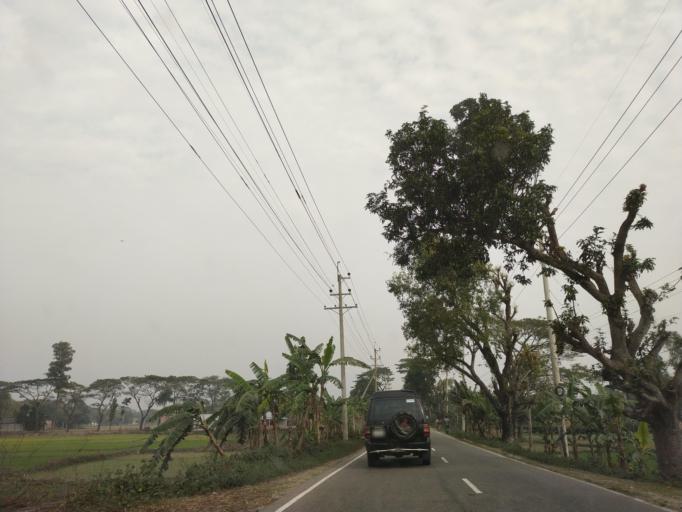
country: BD
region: Dhaka
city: Narsingdi
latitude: 23.9947
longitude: 90.7372
